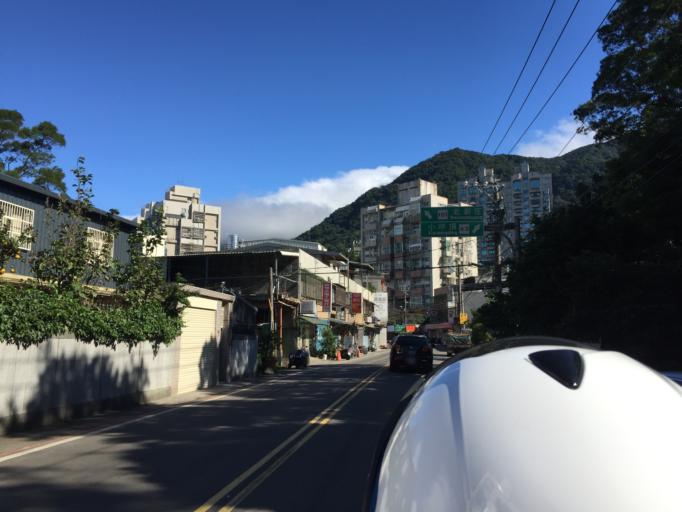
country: TW
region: Taipei
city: Taipei
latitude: 25.1855
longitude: 121.4812
